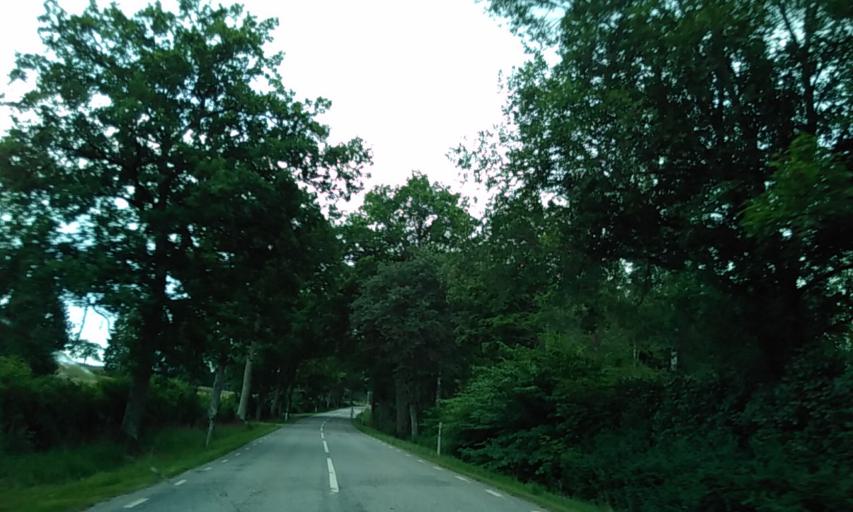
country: SE
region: Vaestra Goetaland
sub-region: Grastorps Kommun
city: Graestorp
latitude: 58.4749
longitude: 12.8264
